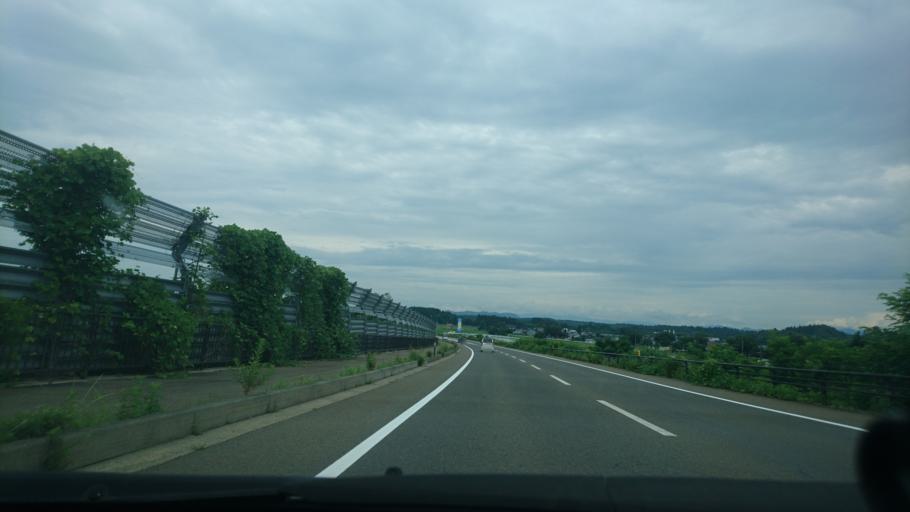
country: JP
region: Akita
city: Omagari
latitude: 39.4932
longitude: 140.4501
